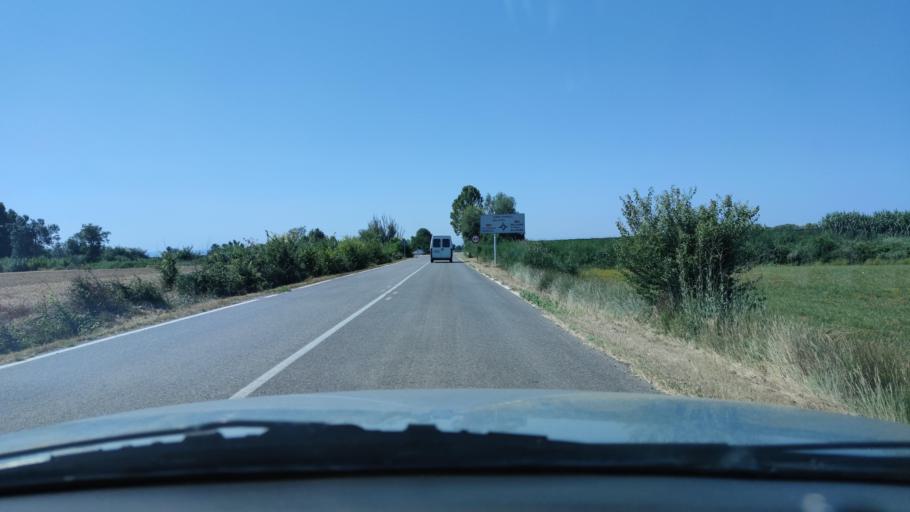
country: ES
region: Catalonia
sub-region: Provincia de Lleida
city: Penelles
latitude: 41.7309
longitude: 0.9829
